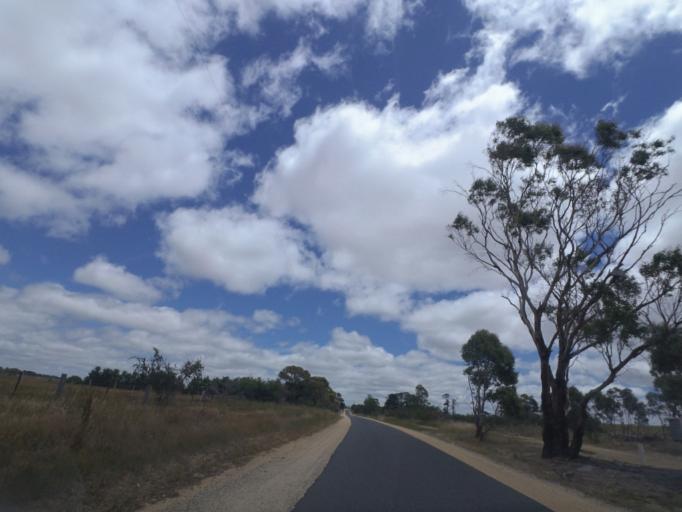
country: AU
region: Victoria
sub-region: Moorabool
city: Bacchus Marsh
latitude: -37.6529
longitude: 144.3151
